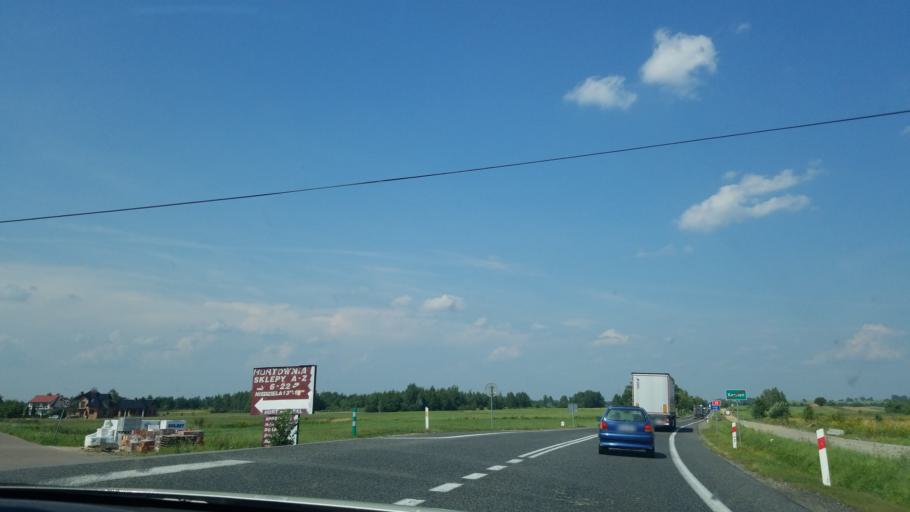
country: PL
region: Subcarpathian Voivodeship
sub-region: Powiat nizanski
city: Jezowe
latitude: 50.3569
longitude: 22.1229
